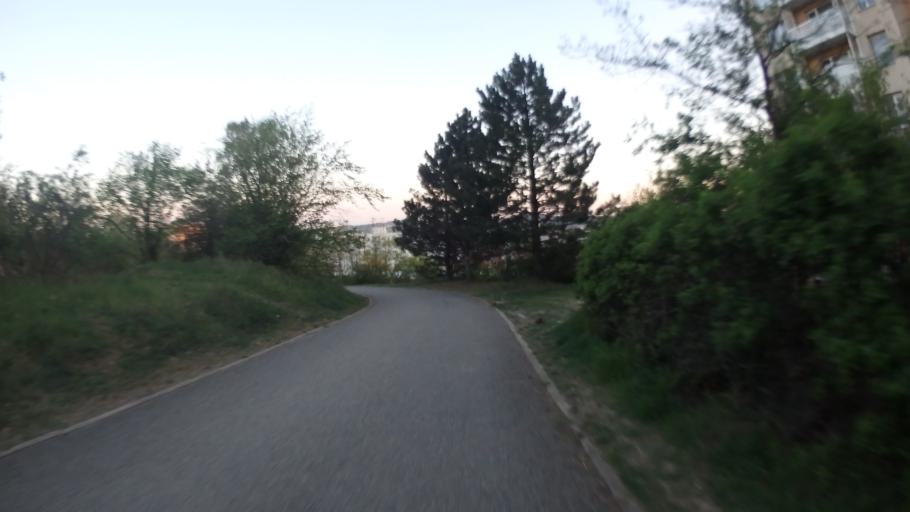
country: CZ
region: South Moravian
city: Ostopovice
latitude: 49.1783
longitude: 16.5559
